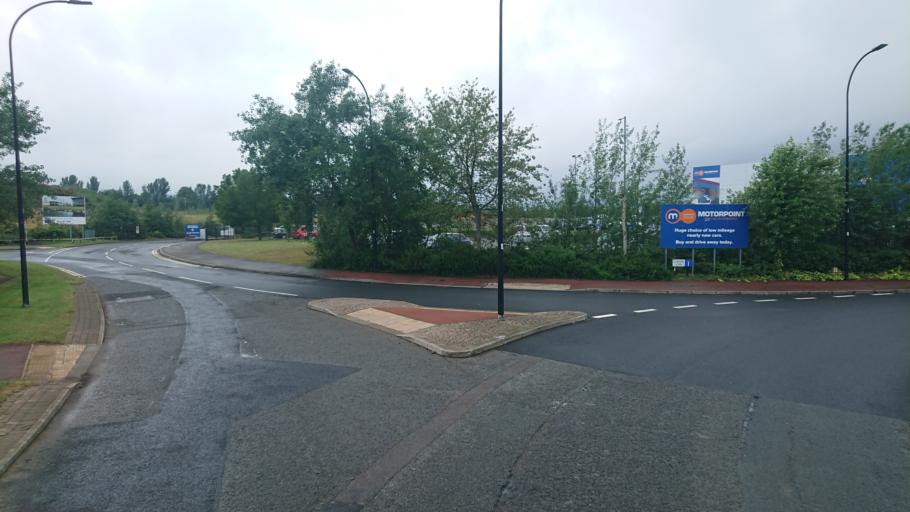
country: GB
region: England
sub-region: Rotherham
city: Orgreave
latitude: 53.3962
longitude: -1.3999
